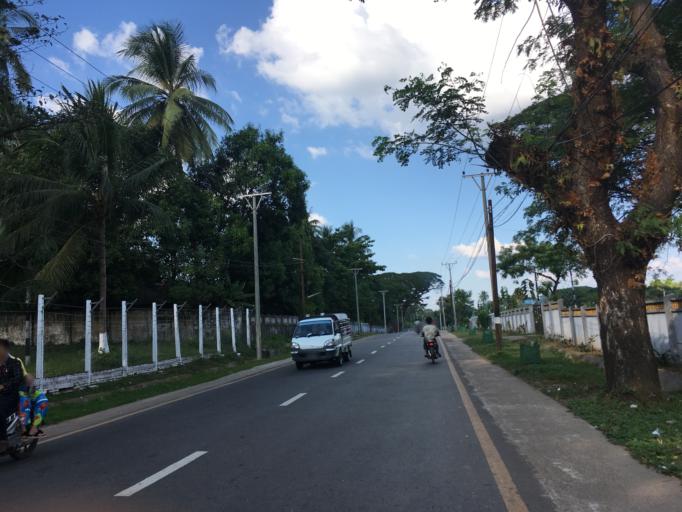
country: MM
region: Mon
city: Mawlamyine
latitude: 16.4410
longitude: 97.6169
